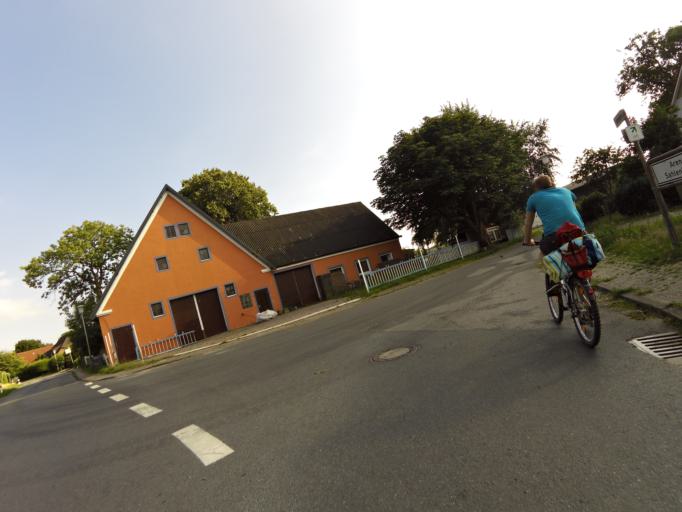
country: DE
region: Lower Saxony
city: Nordholz
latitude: 53.8192
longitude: 8.5908
